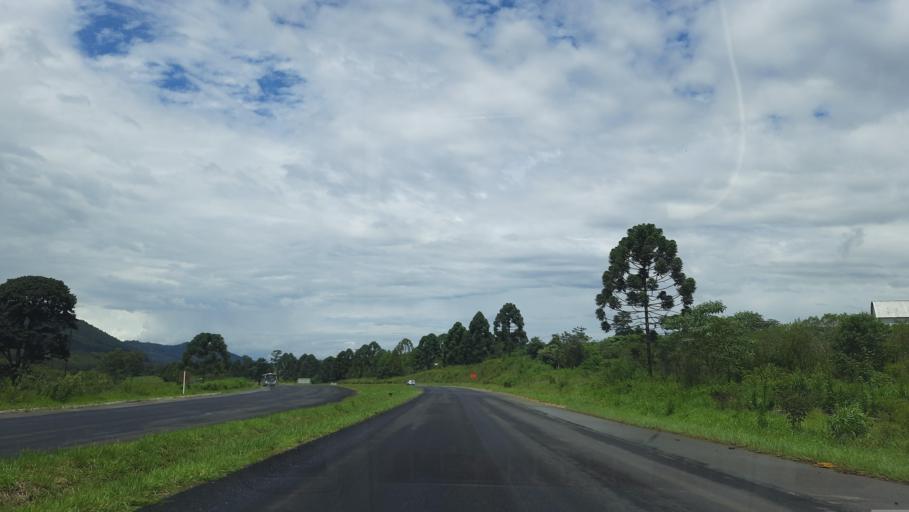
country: BR
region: Minas Gerais
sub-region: Pocos De Caldas
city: Pocos de Caldas
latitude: -21.8219
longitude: -46.6664
